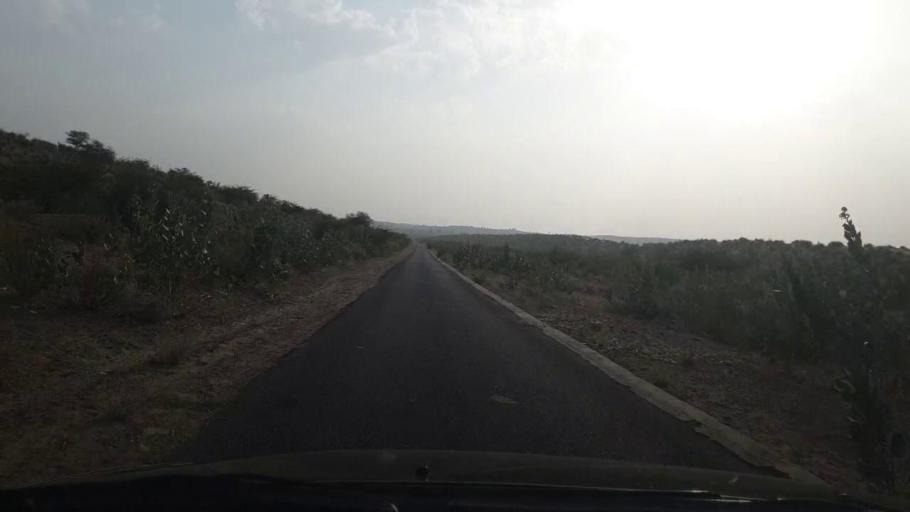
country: PK
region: Sindh
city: Islamkot
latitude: 25.0708
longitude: 70.4699
